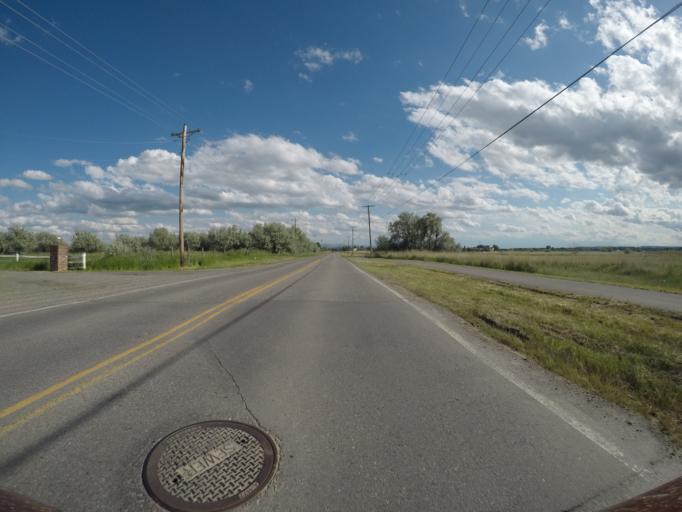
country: US
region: Montana
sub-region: Yellowstone County
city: Billings
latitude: 45.7951
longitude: -108.6527
